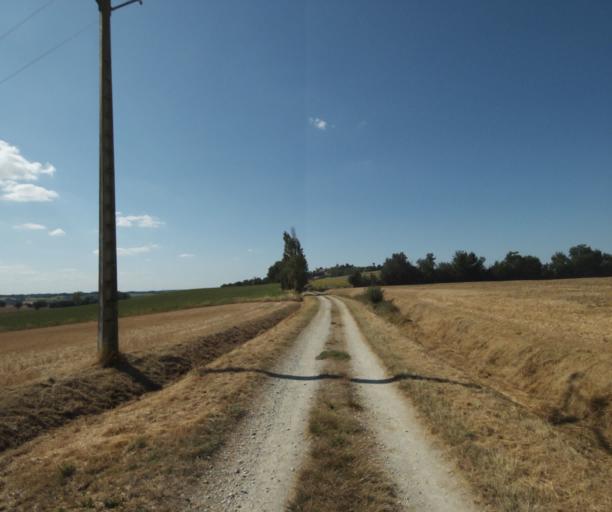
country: FR
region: Midi-Pyrenees
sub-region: Departement de la Haute-Garonne
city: Saint-Felix-Lauragais
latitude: 43.4808
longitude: 1.9079
